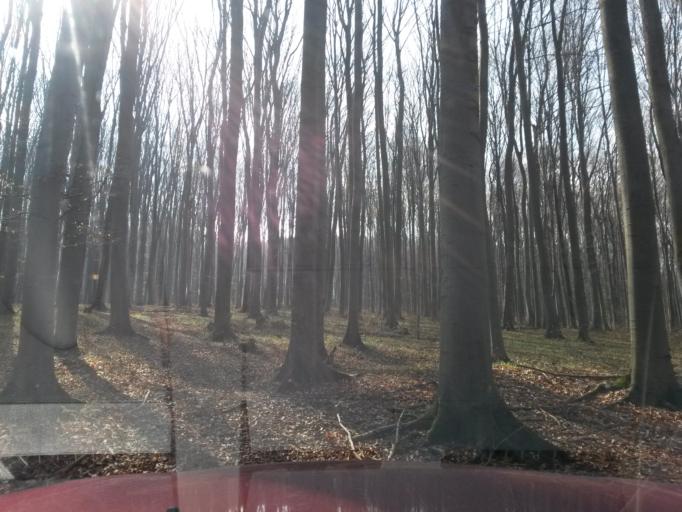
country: SK
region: Presovsky
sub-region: Okres Presov
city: Presov
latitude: 48.9344
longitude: 21.1514
